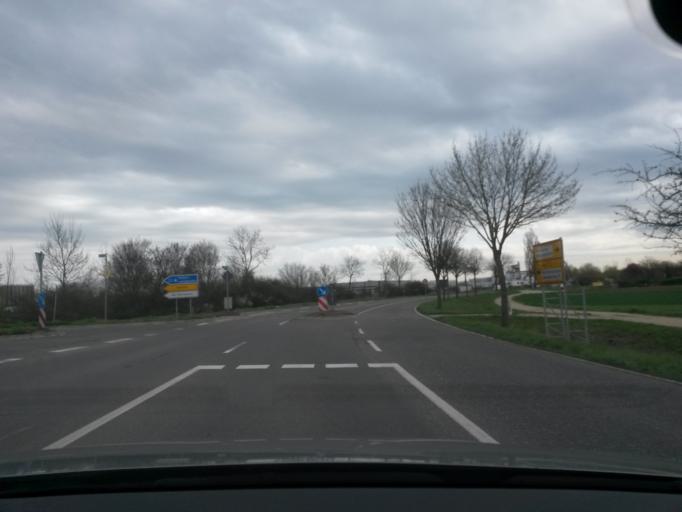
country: DE
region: Rheinland-Pfalz
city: Worms
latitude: 49.6570
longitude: 8.3441
